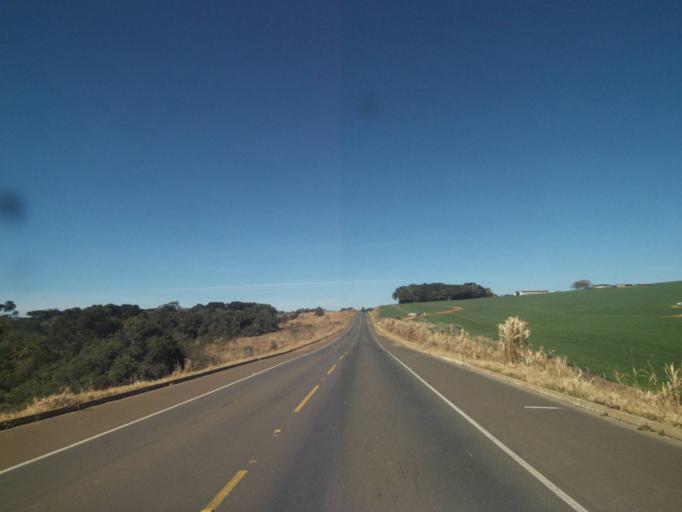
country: BR
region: Parana
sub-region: Tibagi
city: Tibagi
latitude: -24.5351
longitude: -50.4473
